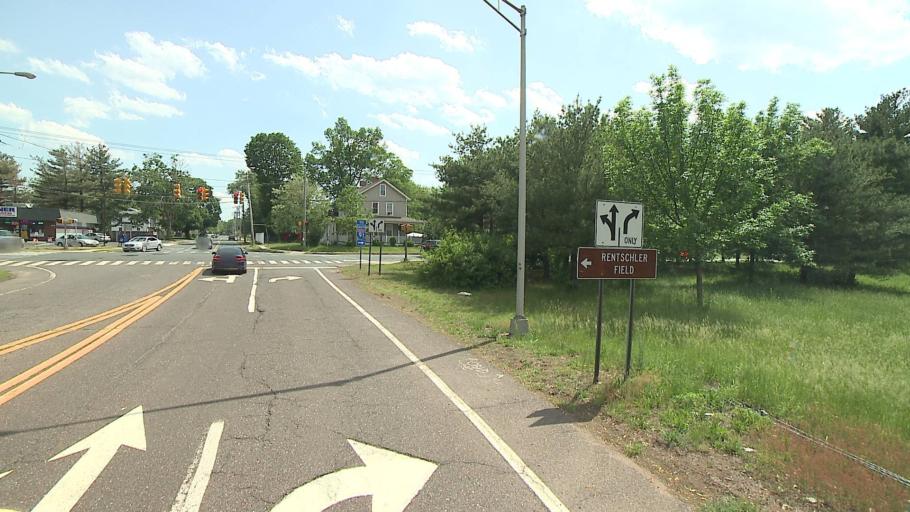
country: US
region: Connecticut
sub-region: Hartford County
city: East Hartford
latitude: 41.7621
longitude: -72.6345
